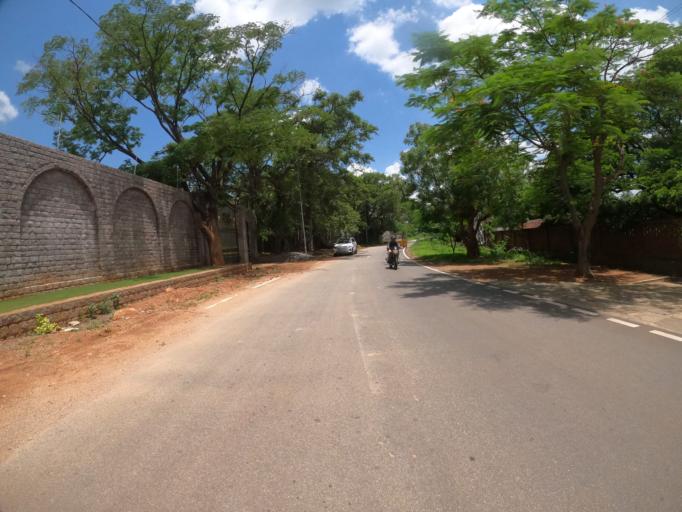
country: IN
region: Telangana
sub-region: Rangareddi
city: Sriramnagar
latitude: 17.3670
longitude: 78.3253
